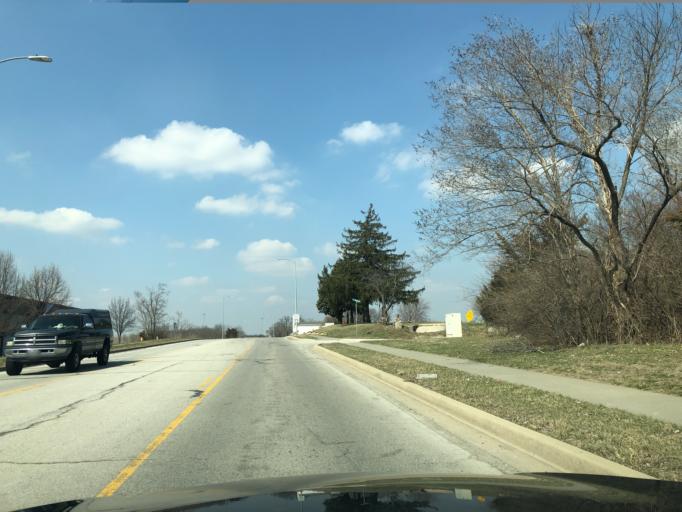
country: US
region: Missouri
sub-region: Platte County
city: Riverside
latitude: 39.1838
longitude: -94.6133
